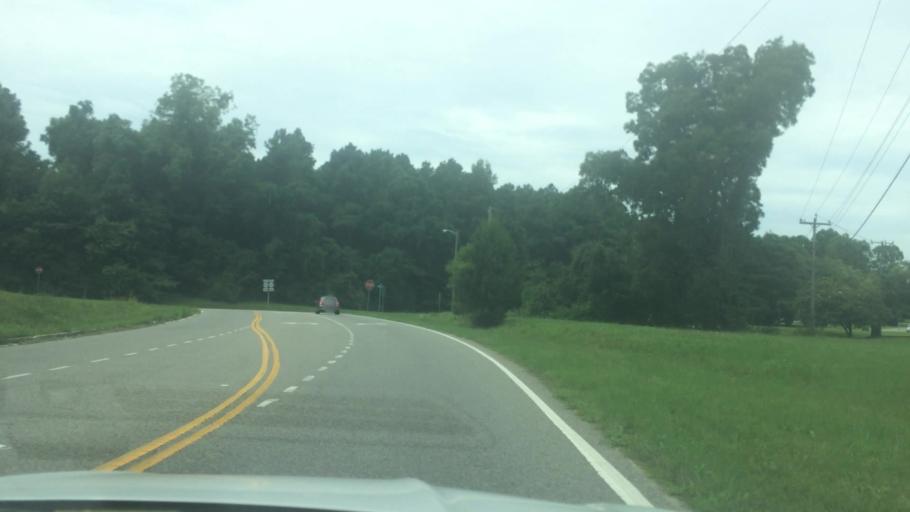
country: US
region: Virginia
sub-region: James City County
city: Williamsburg
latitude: 37.2982
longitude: -76.7401
